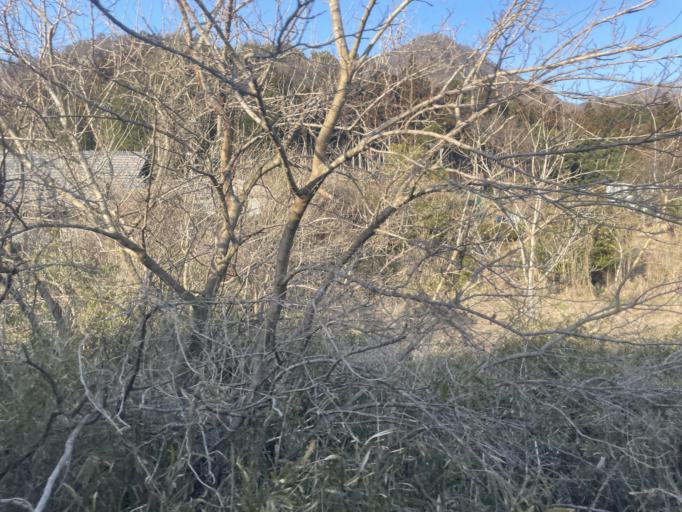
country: JP
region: Gunma
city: Nakanojomachi
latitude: 36.5680
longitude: 138.8873
